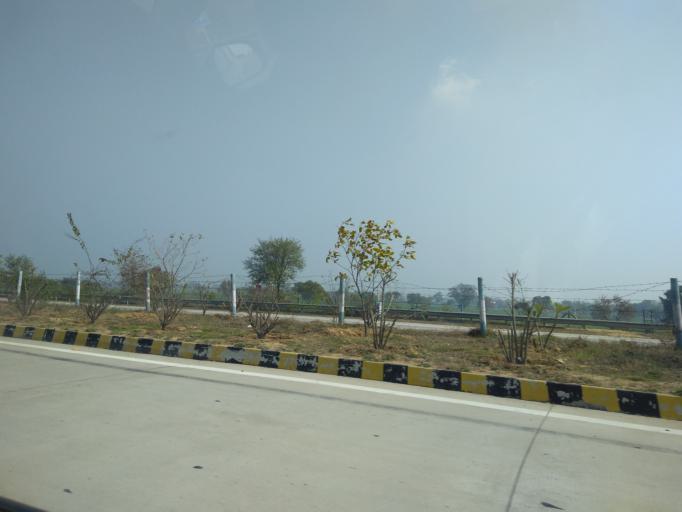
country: IN
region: Uttar Pradesh
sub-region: Mathura
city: Vrindavan
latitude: 27.6178
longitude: 77.7412
